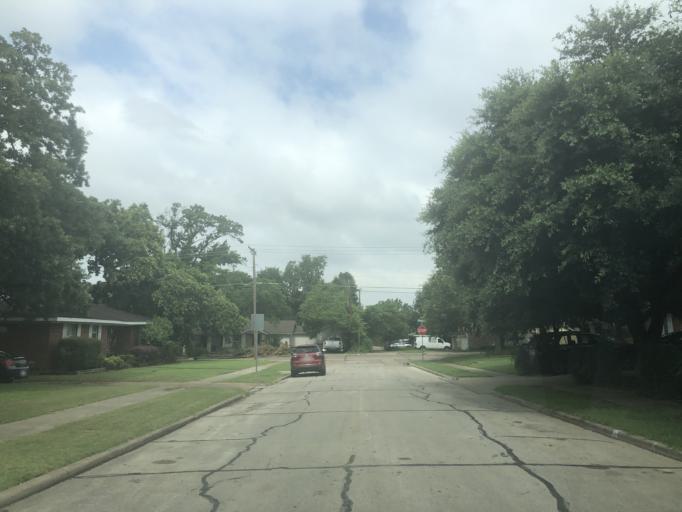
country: US
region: Texas
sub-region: Dallas County
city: Irving
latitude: 32.8052
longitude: -96.9624
